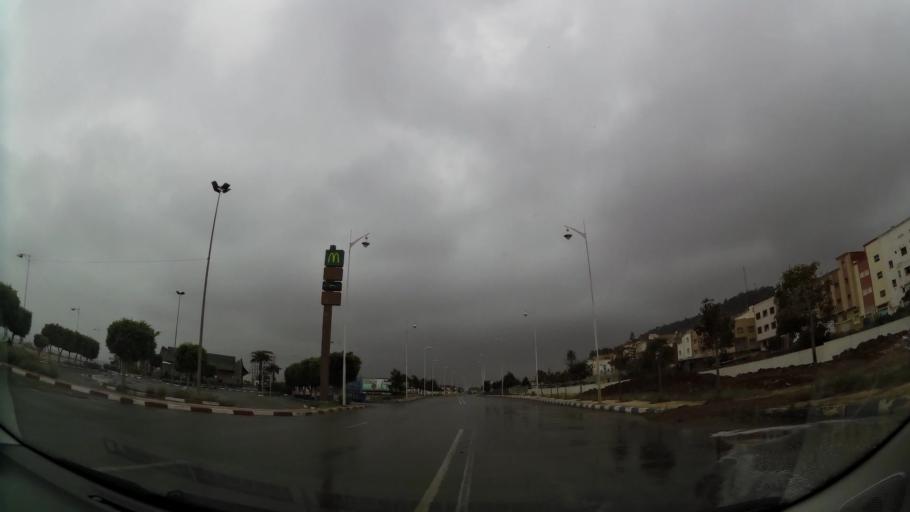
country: MA
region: Oriental
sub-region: Nador
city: Nador
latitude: 35.1881
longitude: -2.9262
